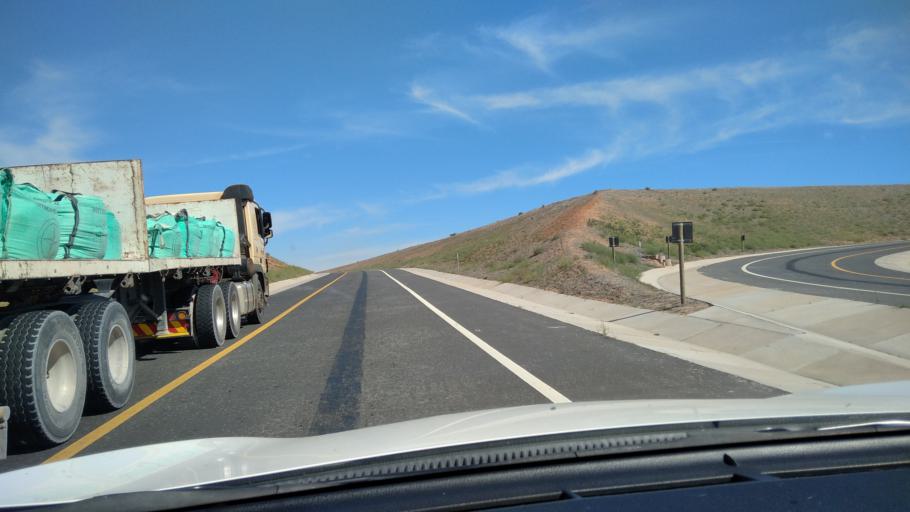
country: ZA
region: Western Cape
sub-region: West Coast District Municipality
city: Malmesbury
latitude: -33.4145
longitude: 18.7143
